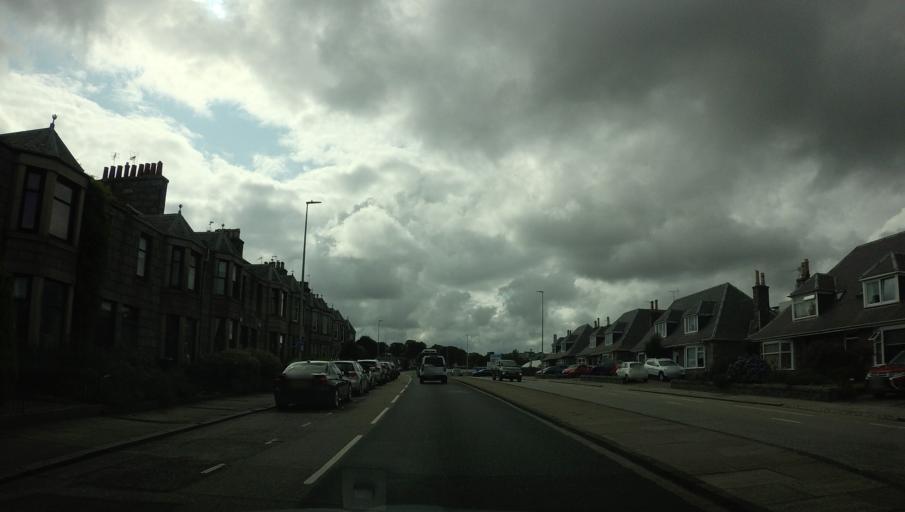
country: GB
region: Scotland
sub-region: Aberdeen City
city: Aberdeen
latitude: 57.1524
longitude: -2.1305
